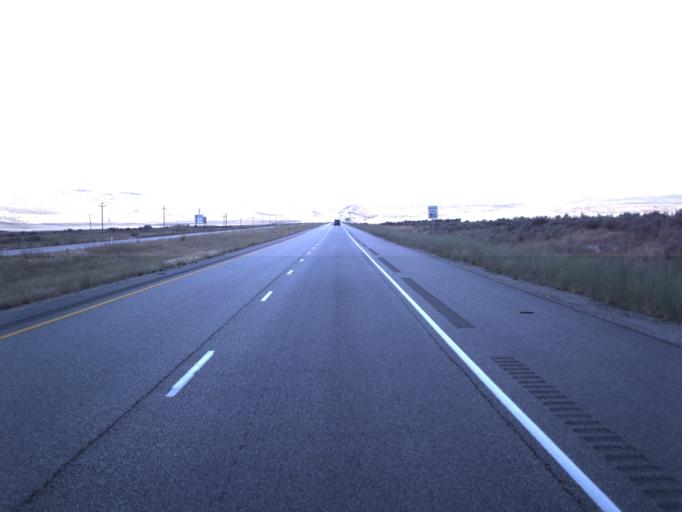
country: US
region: Utah
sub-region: Box Elder County
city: Garland
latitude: 41.8889
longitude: -112.5044
